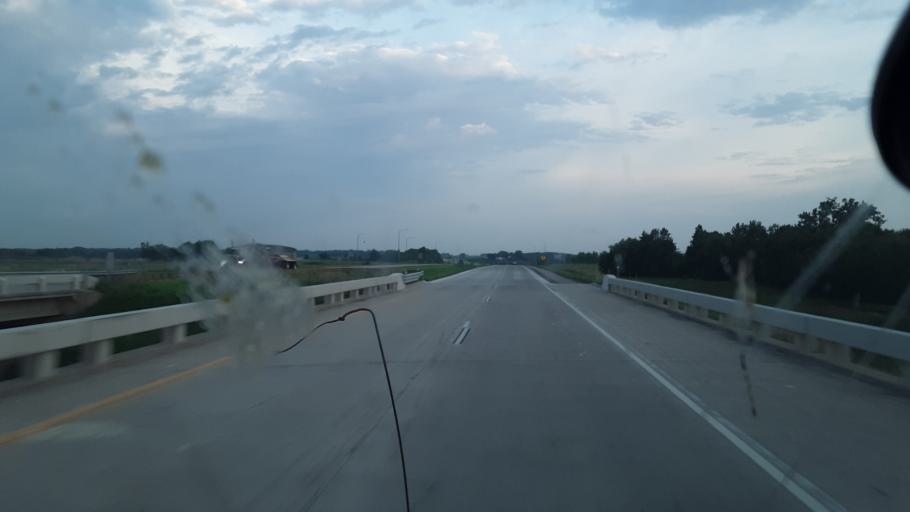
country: US
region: Minnesota
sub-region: Freeborn County
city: Albert Lea
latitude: 43.6878
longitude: -93.3585
